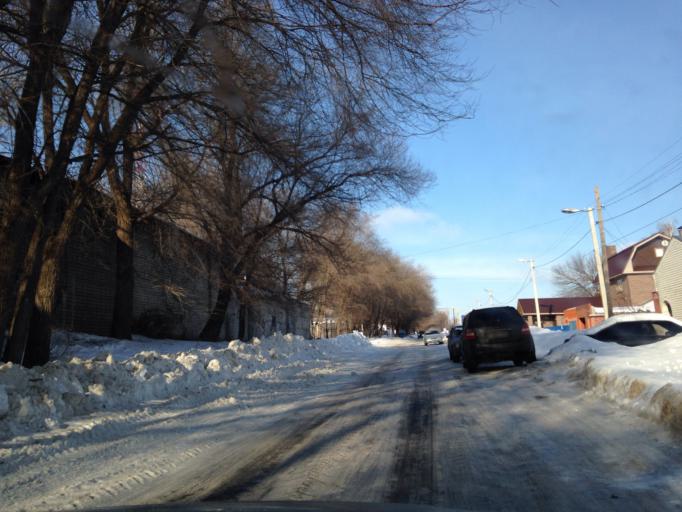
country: RU
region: Ulyanovsk
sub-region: Ulyanovskiy Rayon
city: Ulyanovsk
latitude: 54.3391
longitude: 48.5456
